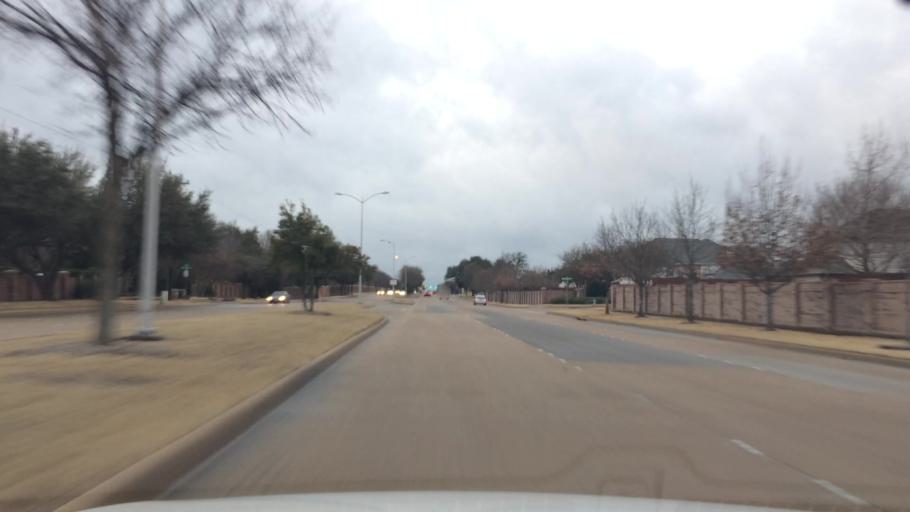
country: US
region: Texas
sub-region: Collin County
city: Frisco
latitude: 33.0986
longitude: -96.7716
